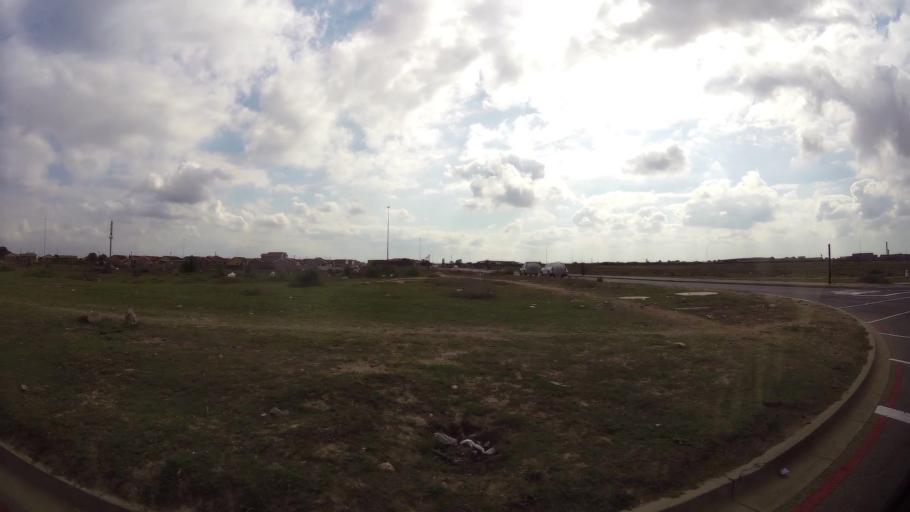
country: ZA
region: Eastern Cape
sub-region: Nelson Mandela Bay Metropolitan Municipality
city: Port Elizabeth
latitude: -33.8169
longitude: 25.5947
